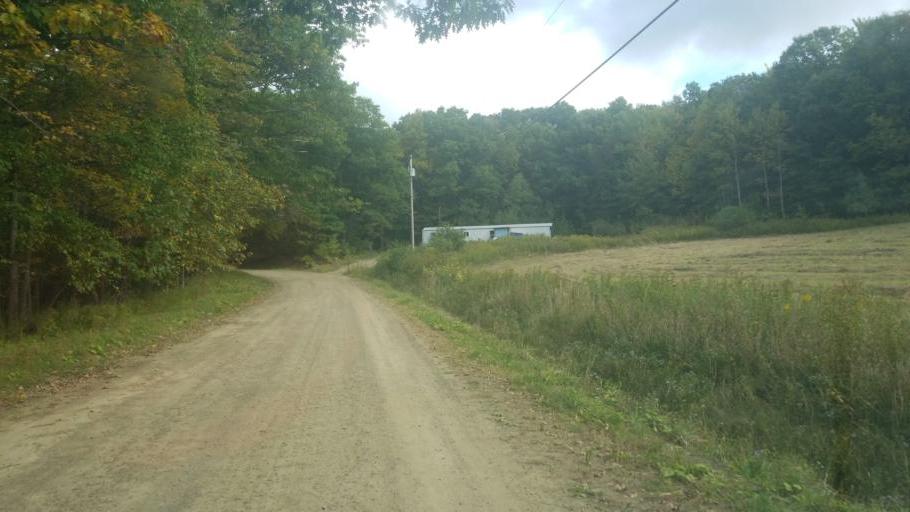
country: US
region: New York
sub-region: Allegany County
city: Cuba
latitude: 42.1395
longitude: -78.3014
